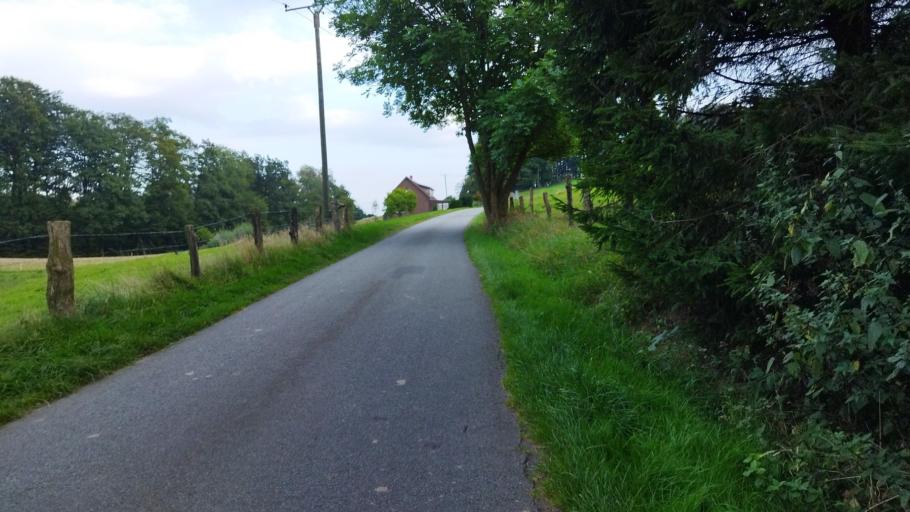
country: DE
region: Lower Saxony
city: Hagen
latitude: 52.1787
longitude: 8.0065
